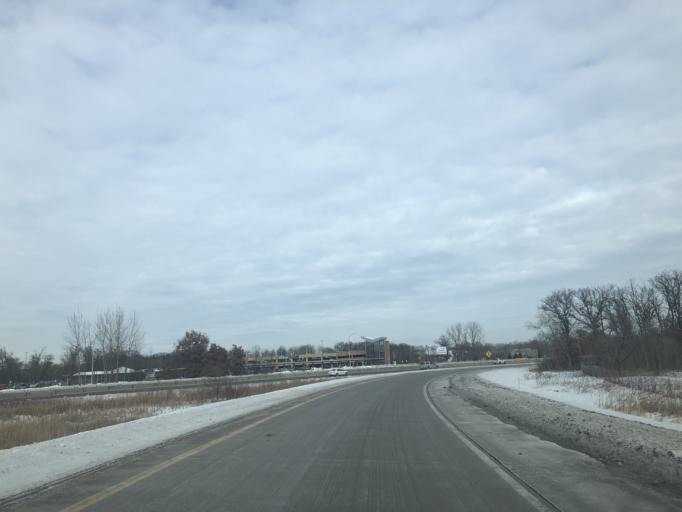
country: US
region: Minnesota
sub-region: Anoka County
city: Lexington
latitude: 45.1439
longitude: -93.1828
